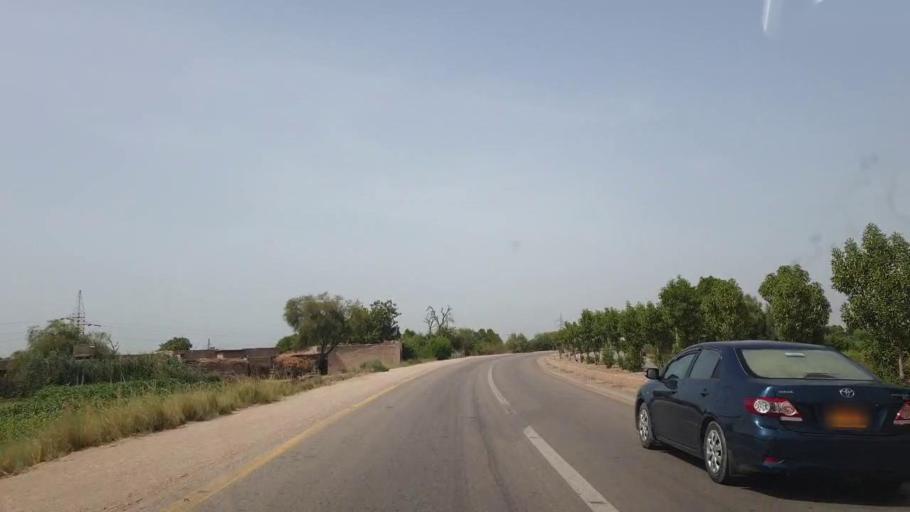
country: PK
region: Sindh
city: Sakrand
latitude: 26.1925
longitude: 68.2914
